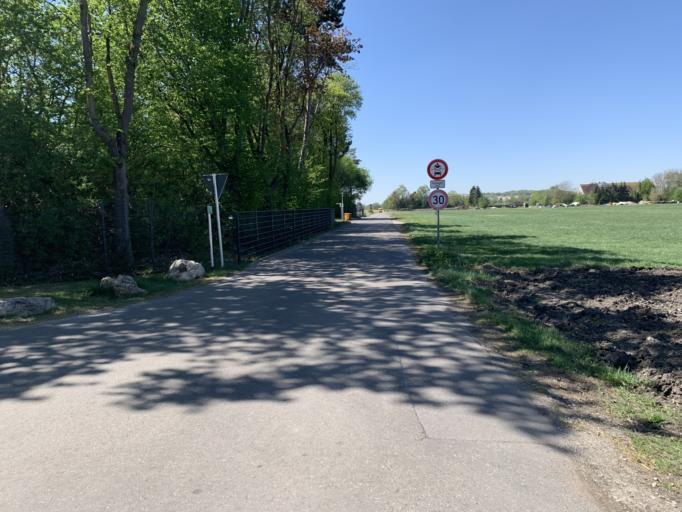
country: DE
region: Bavaria
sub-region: Swabia
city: Augsburg
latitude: 48.4136
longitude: 10.9194
